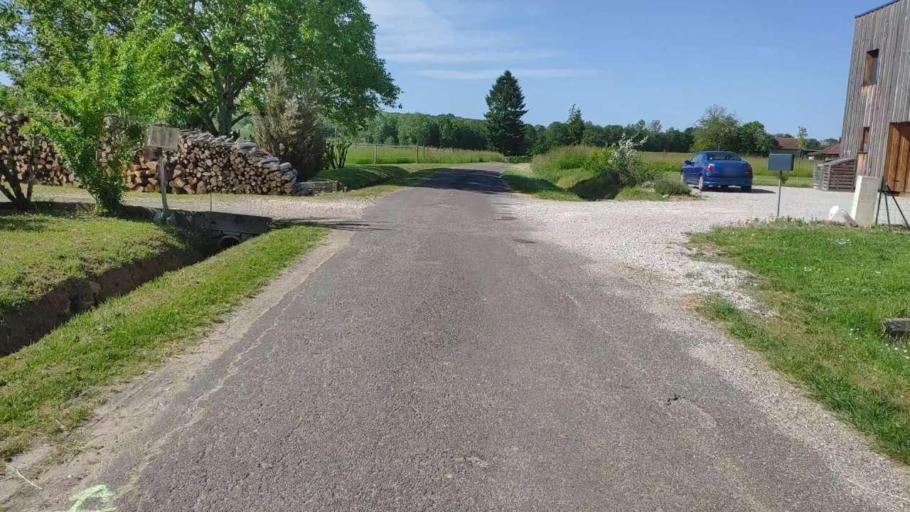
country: FR
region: Franche-Comte
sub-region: Departement du Jura
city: Bletterans
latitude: 46.7081
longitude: 5.4654
